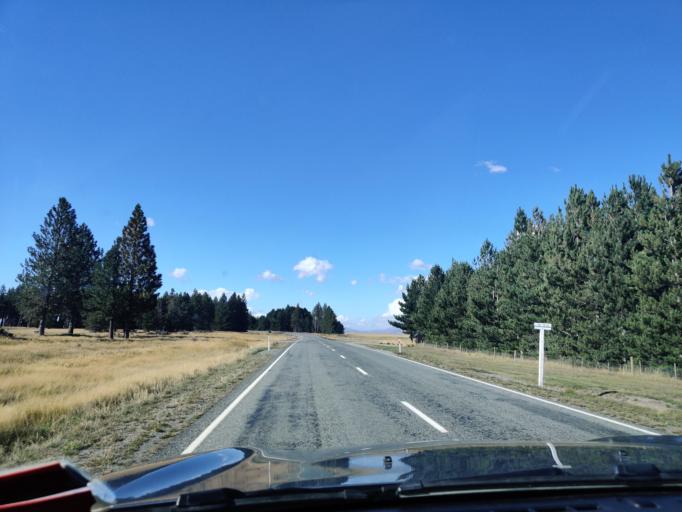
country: NZ
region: Canterbury
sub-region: Timaru District
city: Pleasant Point
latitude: -44.1819
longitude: 170.3149
